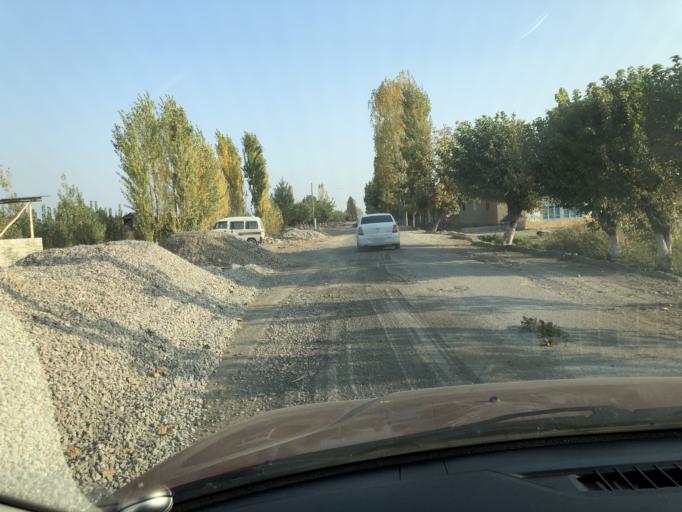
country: UZ
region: Namangan
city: Uychi
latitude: 41.0661
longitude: 71.9858
